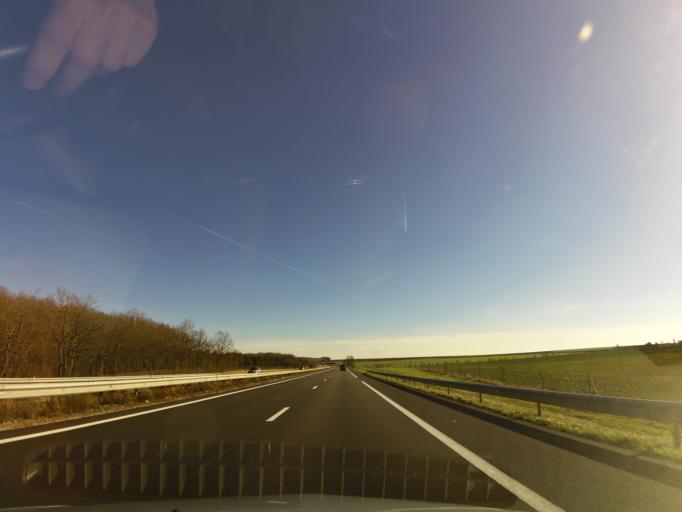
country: FR
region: Bourgogne
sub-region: Departement de l'Yonne
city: Vermenton
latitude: 47.7029
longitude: 3.8036
